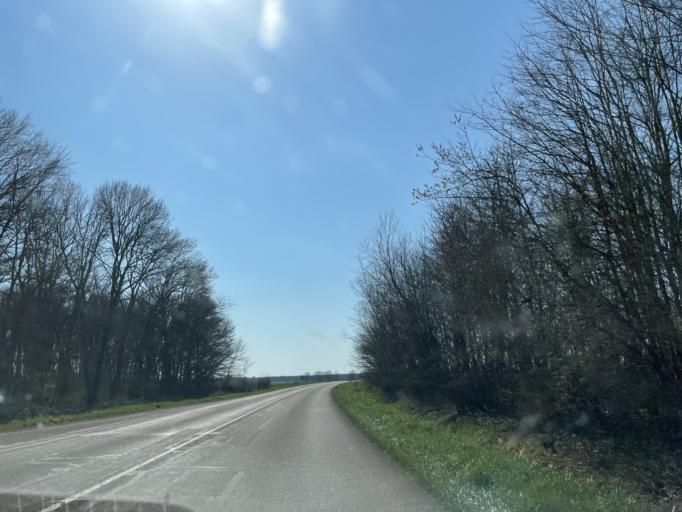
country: FR
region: Bourgogne
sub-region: Departement de la Cote-d'Or
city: Semur-en-Auxois
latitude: 47.4595
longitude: 4.3435
